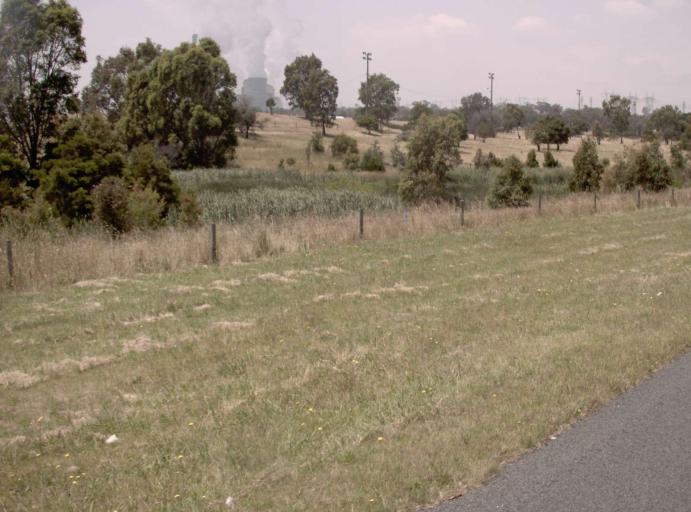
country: AU
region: Victoria
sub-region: Latrobe
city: Traralgon
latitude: -38.2442
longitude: 146.5461
